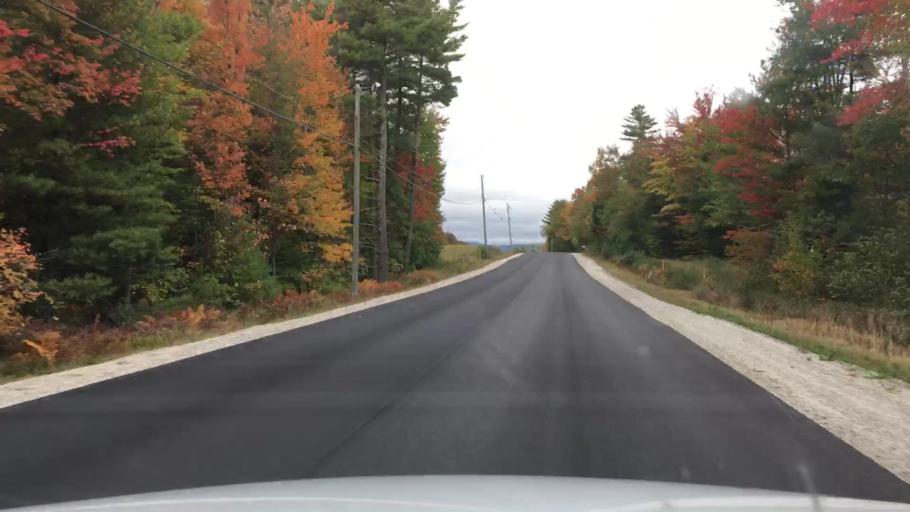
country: US
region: Maine
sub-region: Oxford County
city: Bethel
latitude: 44.3034
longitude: -70.7505
